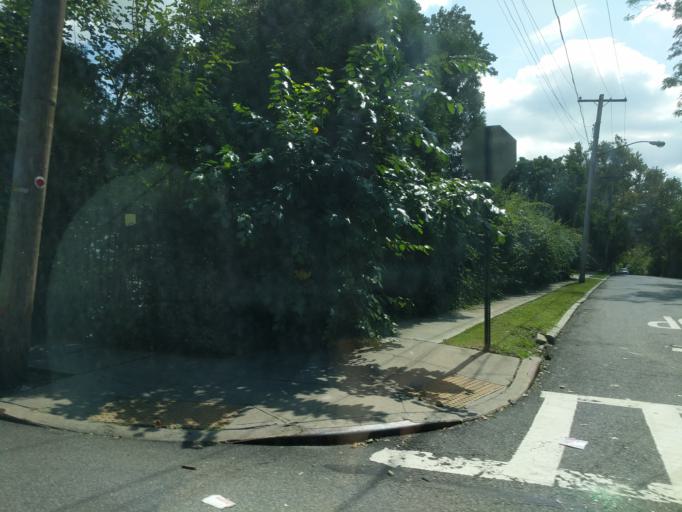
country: US
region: New Jersey
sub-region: Hudson County
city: Bayonne
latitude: 40.6389
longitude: -74.1048
